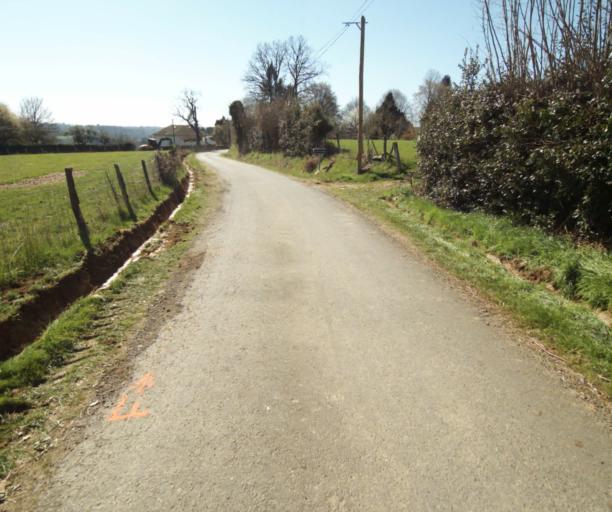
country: FR
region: Limousin
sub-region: Departement de la Correze
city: Saint-Clement
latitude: 45.3519
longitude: 1.6615
